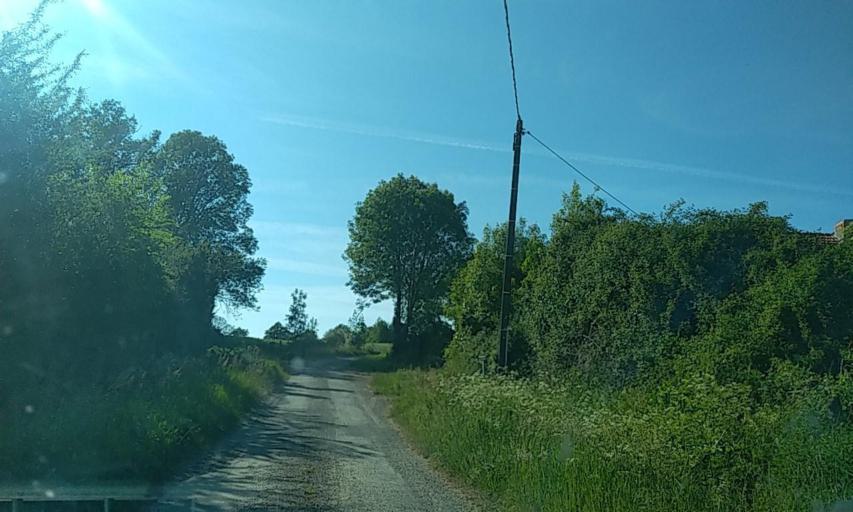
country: FR
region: Poitou-Charentes
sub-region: Departement des Deux-Sevres
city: Boisme
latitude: 46.7832
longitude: -0.4380
